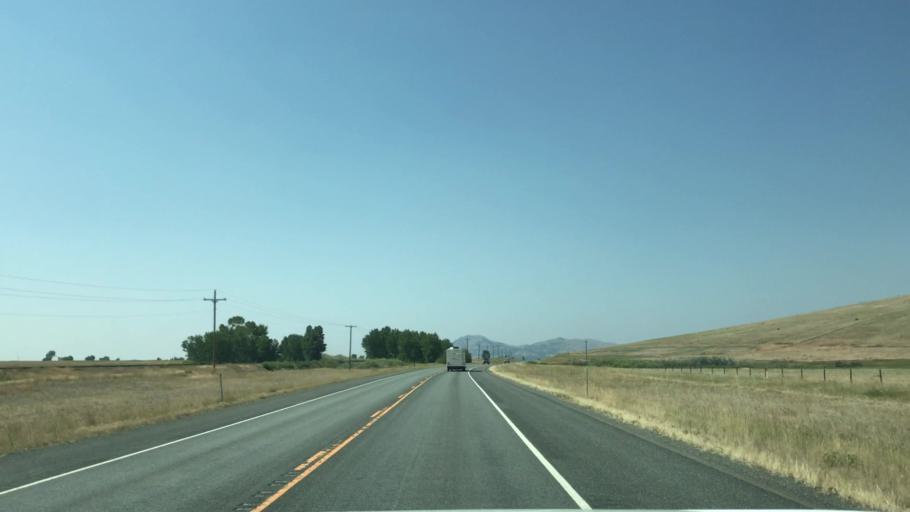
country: US
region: Montana
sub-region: Broadwater County
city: Townsend
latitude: 46.4662
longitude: -111.6476
